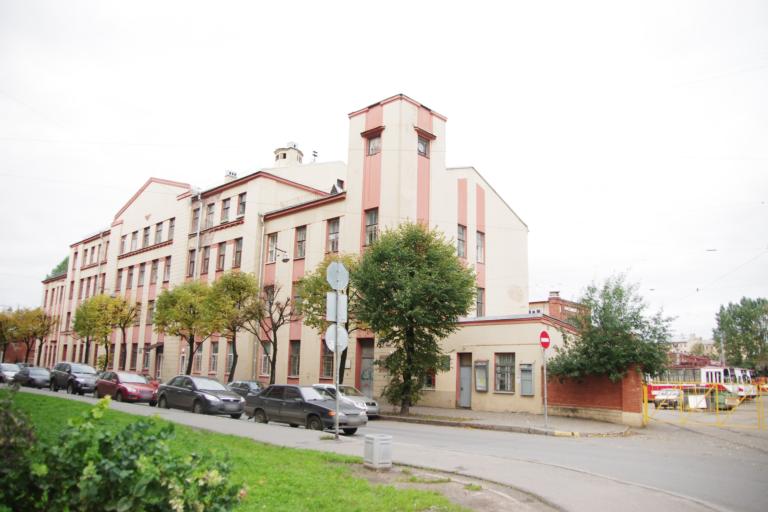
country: RU
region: St.-Petersburg
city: Petrogradka
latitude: 59.9605
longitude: 30.3309
